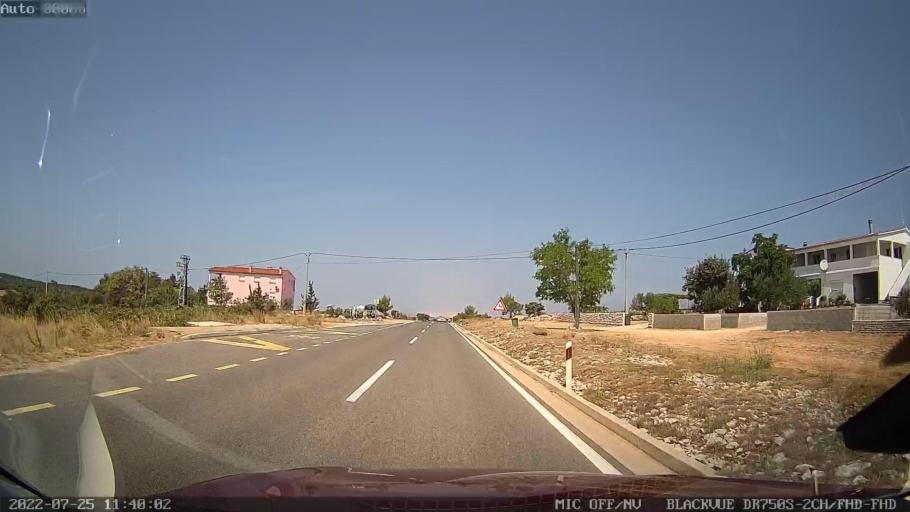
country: HR
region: Zadarska
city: Razanac
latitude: 44.2606
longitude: 15.3653
